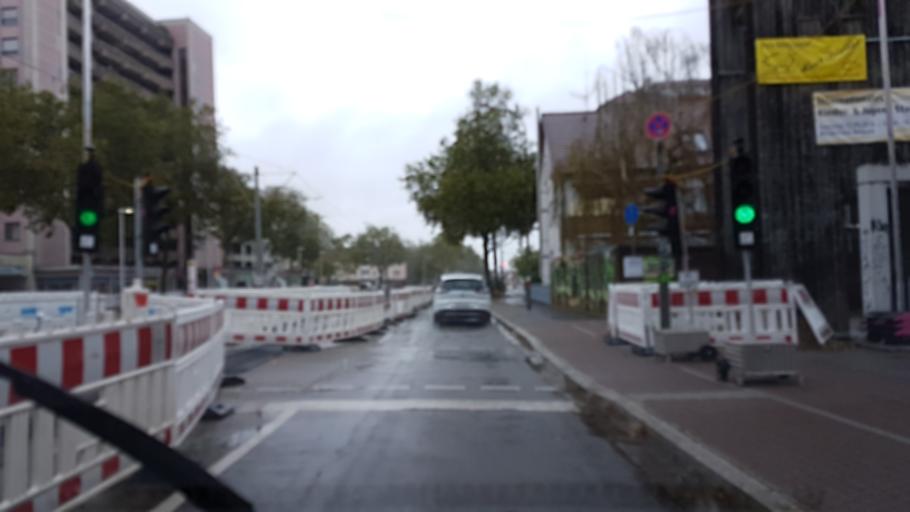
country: DE
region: Baden-Wuerttemberg
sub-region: Freiburg Region
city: Freiburg
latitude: 48.0108
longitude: 7.8117
